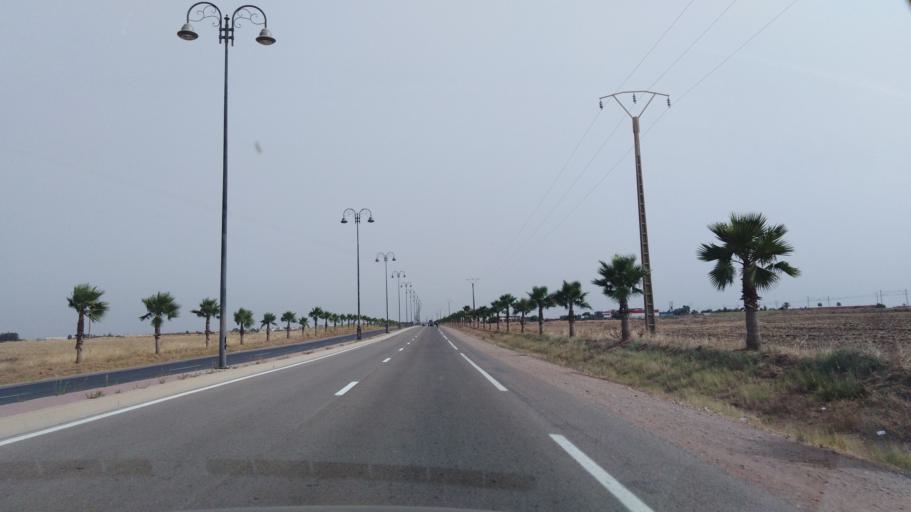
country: MA
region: Chaouia-Ouardigha
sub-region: Settat Province
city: Berrechid
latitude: 33.3037
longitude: -7.6002
